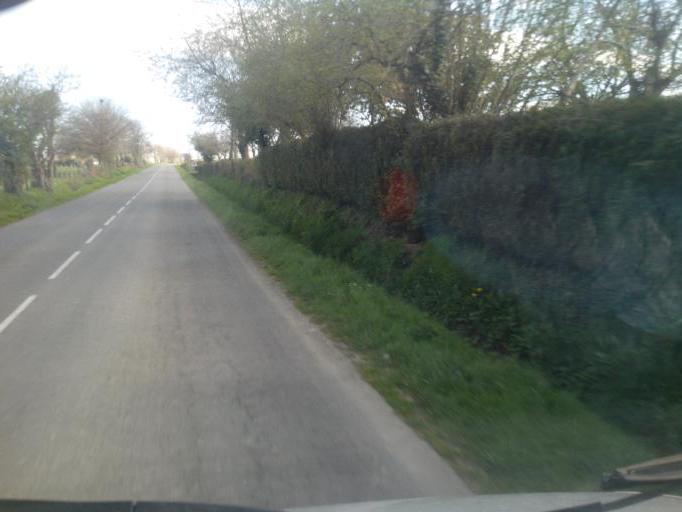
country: FR
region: Brittany
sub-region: Departement d'Ille-et-Vilaine
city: Maure-de-Bretagne
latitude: 47.9156
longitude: -1.9936
